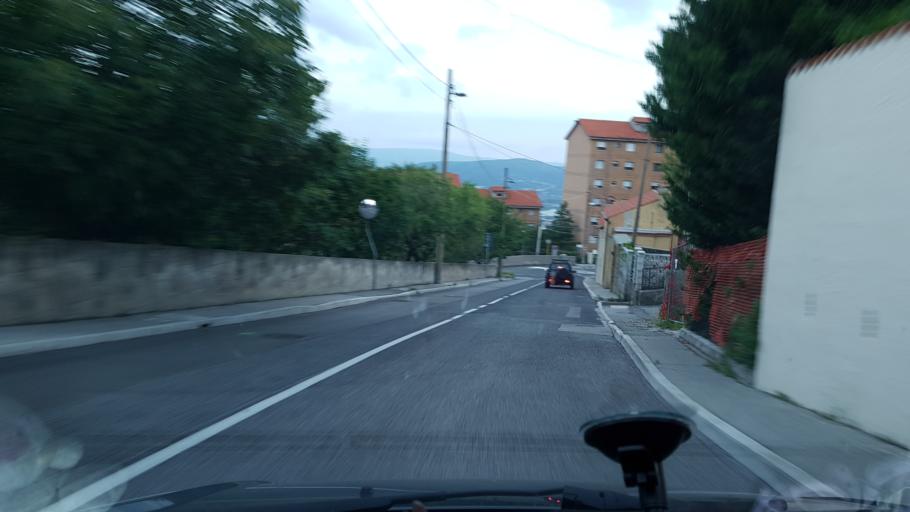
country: IT
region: Friuli Venezia Giulia
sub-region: Provincia di Trieste
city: Domio
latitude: 45.6321
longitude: 13.8234
